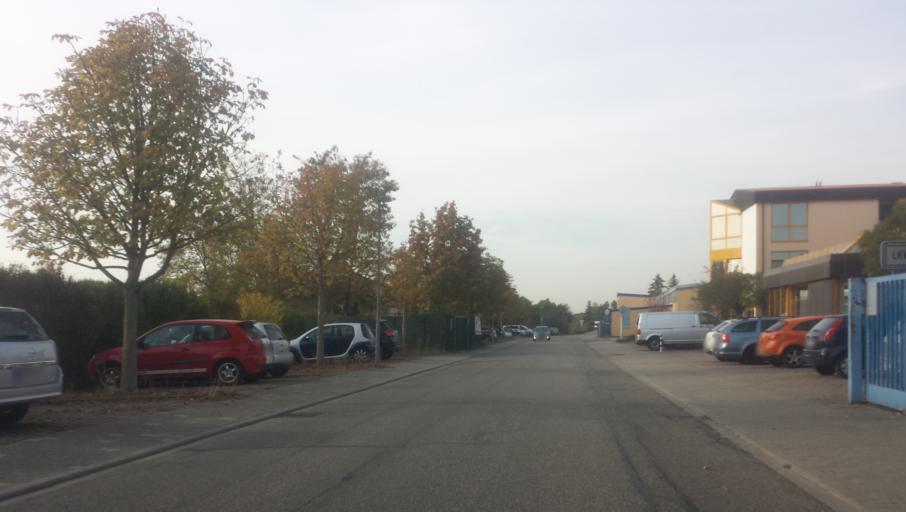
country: DE
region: Baden-Wuerttemberg
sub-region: Karlsruhe Region
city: Neulussheim
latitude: 49.2899
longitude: 8.5078
